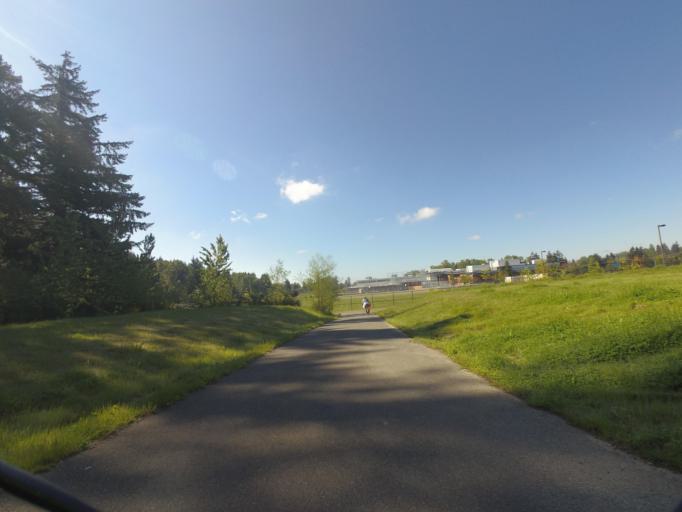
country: US
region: Washington
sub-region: Pierce County
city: Waller
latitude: 47.2113
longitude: -122.4046
